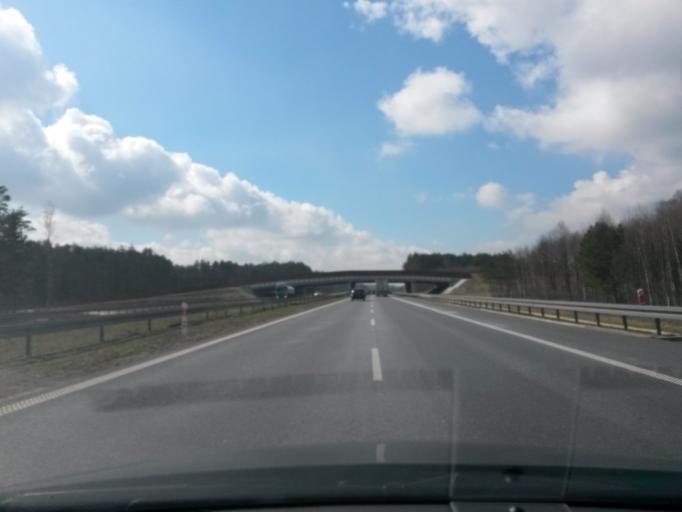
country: PL
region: Lodz Voivodeship
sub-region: Powiat skierniewicki
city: Bolimow
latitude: 52.0547
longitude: 20.1265
